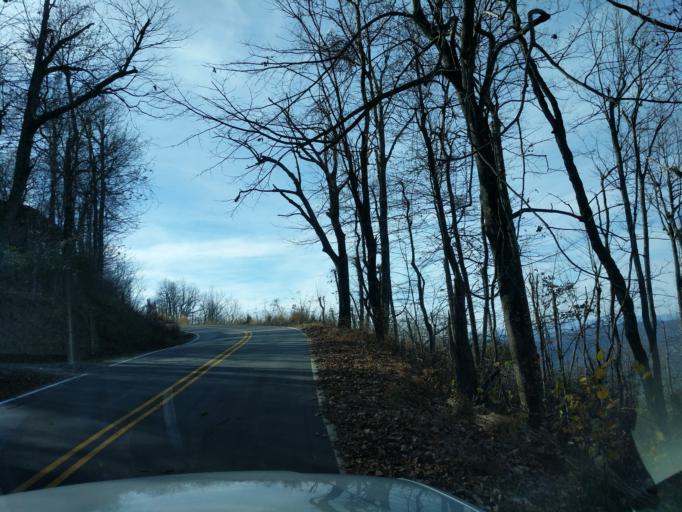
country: US
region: North Carolina
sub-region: Polk County
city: Columbus
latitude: 35.2783
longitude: -82.2254
